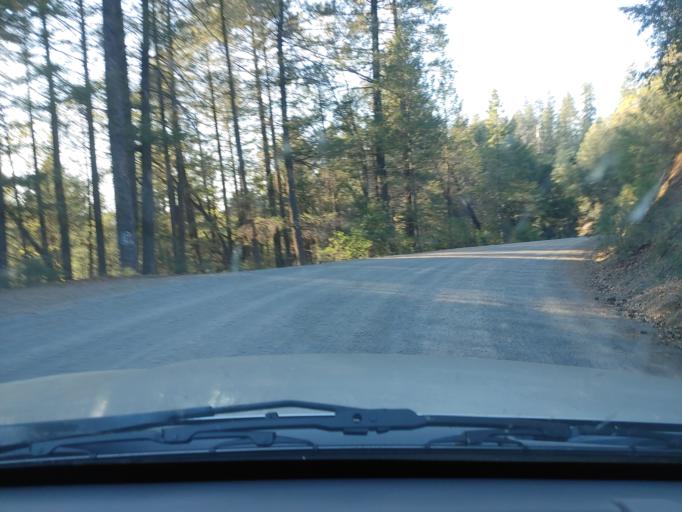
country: US
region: California
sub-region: Shasta County
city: Bella Vista
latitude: 40.8210
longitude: -122.0154
